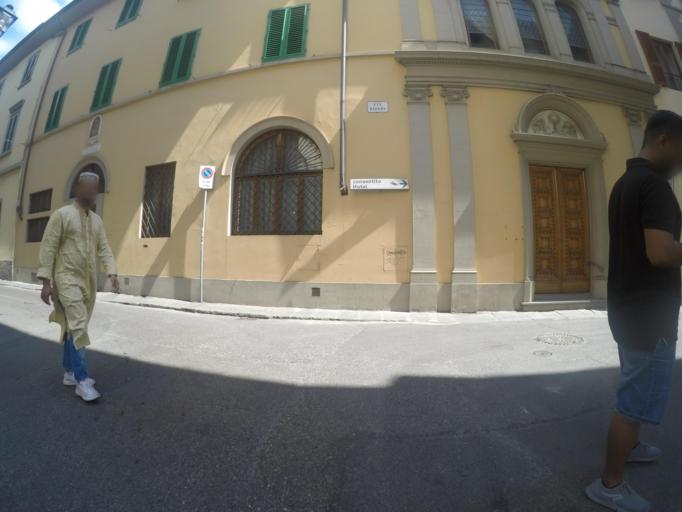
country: IT
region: Tuscany
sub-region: Province of Florence
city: Florence
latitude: 43.7785
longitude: 11.2506
